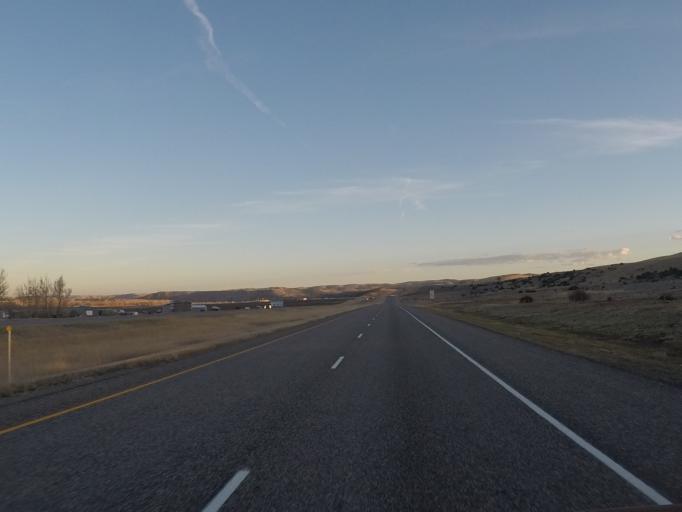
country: US
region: Montana
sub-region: Sweet Grass County
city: Big Timber
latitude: 45.7623
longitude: -109.7879
